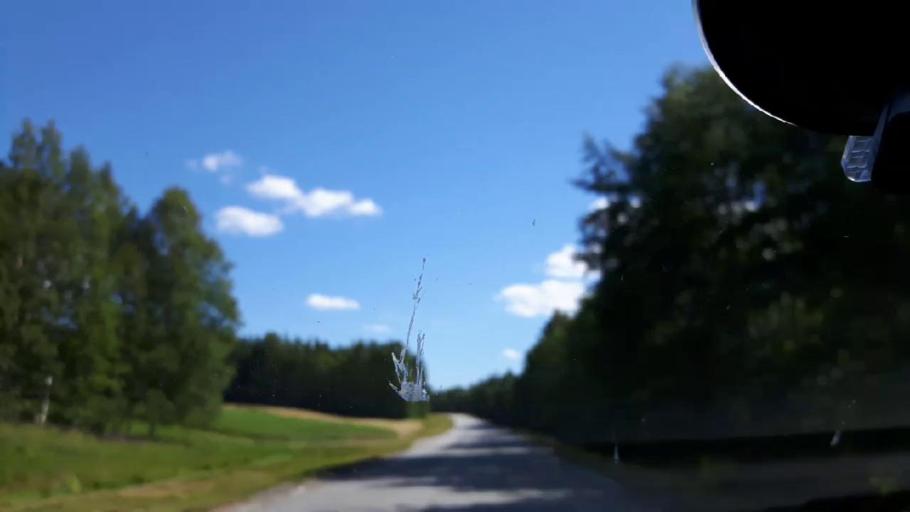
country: SE
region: Vaesternorrland
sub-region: Ange Kommun
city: Fransta
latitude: 62.7122
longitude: 16.3410
